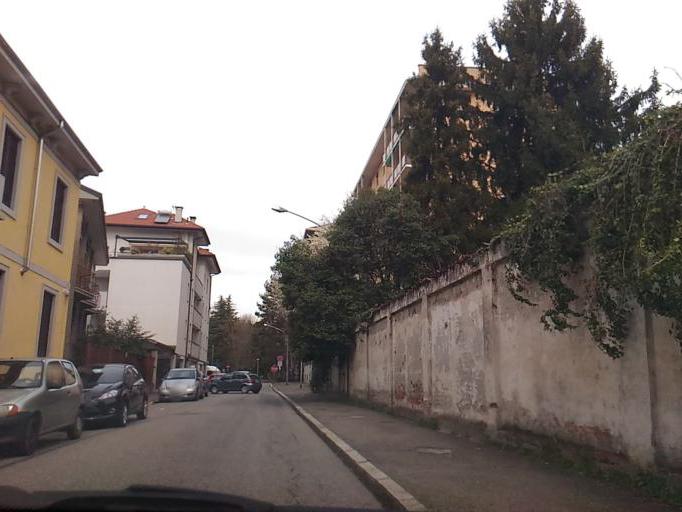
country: IT
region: Lombardy
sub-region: Provincia di Varese
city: Busto Arsizio
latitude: 45.6187
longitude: 8.8453
